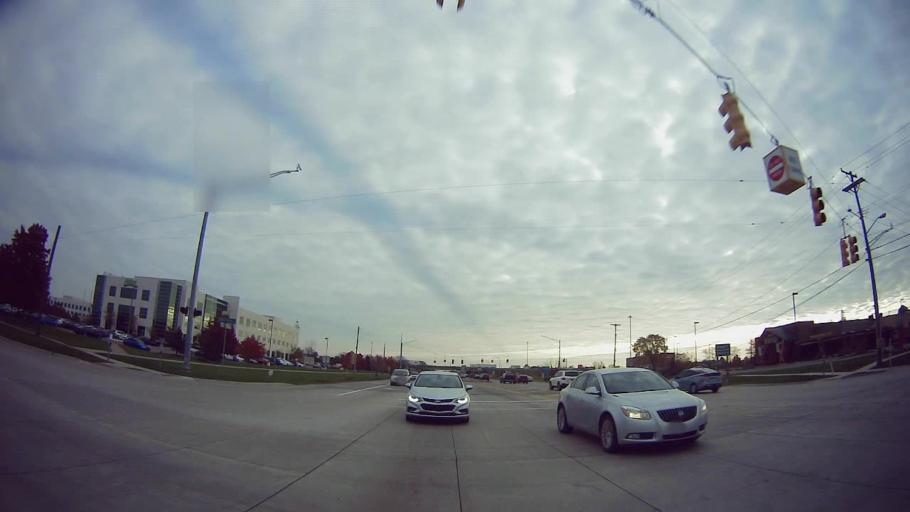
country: US
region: Michigan
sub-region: Oakland County
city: Clawson
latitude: 42.5341
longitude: -83.1199
